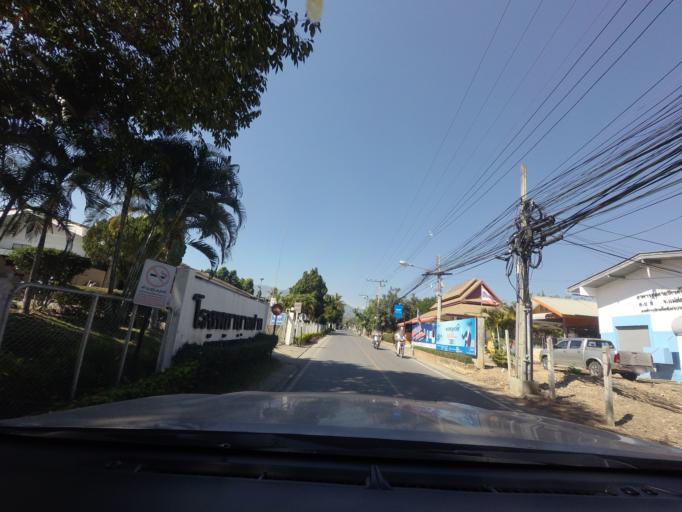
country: TH
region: Chiang Mai
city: Pai
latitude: 19.3620
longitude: 98.4377
